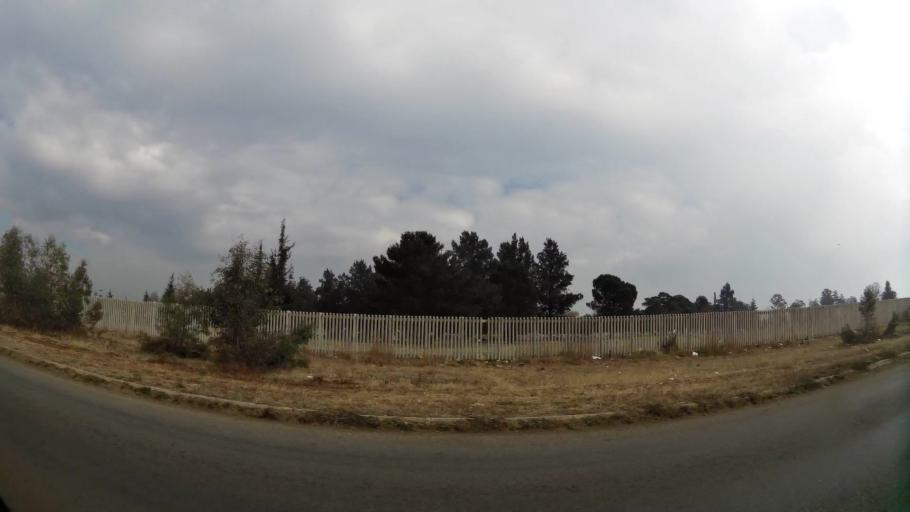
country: ZA
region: Gauteng
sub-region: Sedibeng District Municipality
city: Vanderbijlpark
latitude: -26.6928
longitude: 27.8609
